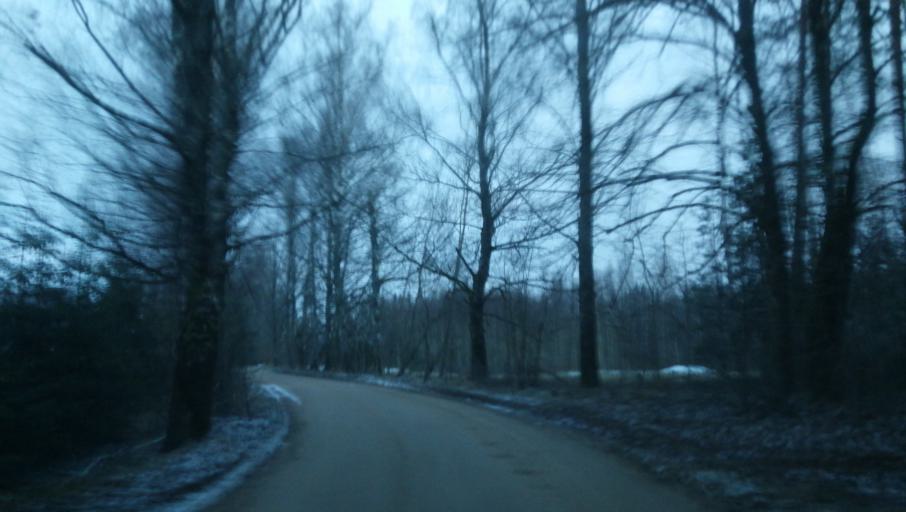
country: LV
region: Garkalne
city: Garkalne
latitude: 57.0186
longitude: 24.3863
